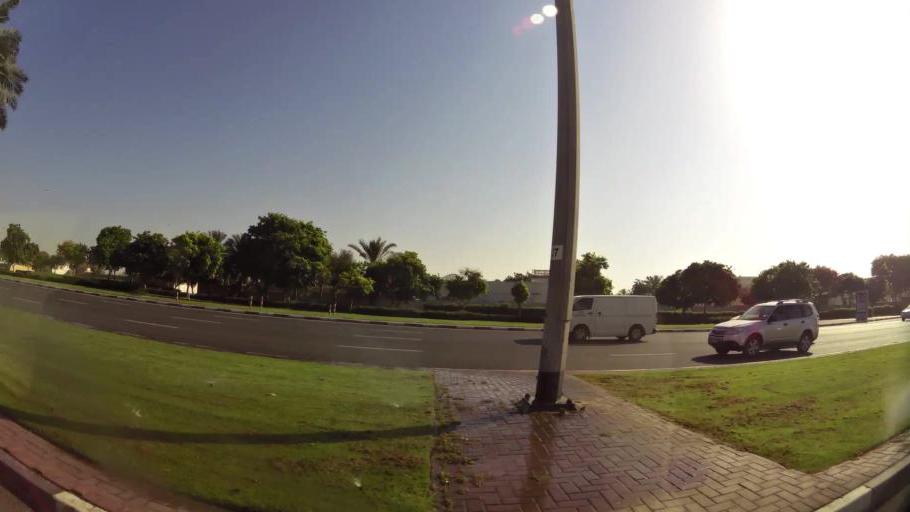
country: AE
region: Ash Shariqah
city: Sharjah
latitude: 25.2671
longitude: 55.3650
